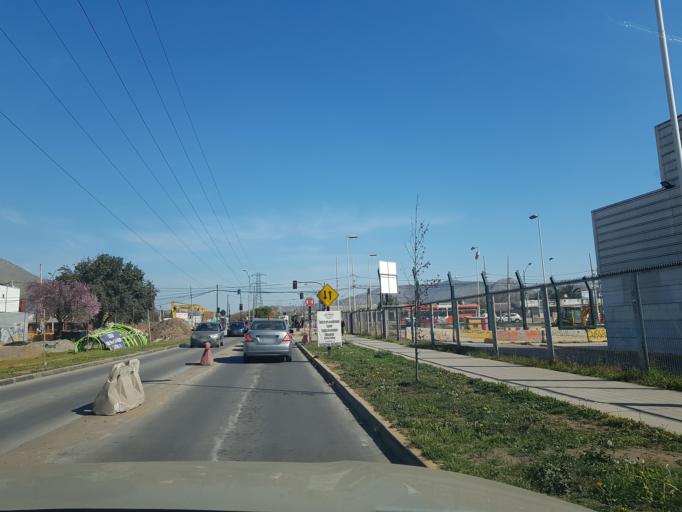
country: CL
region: Santiago Metropolitan
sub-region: Provincia de Santiago
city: Lo Prado
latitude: -33.3660
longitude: -70.7196
